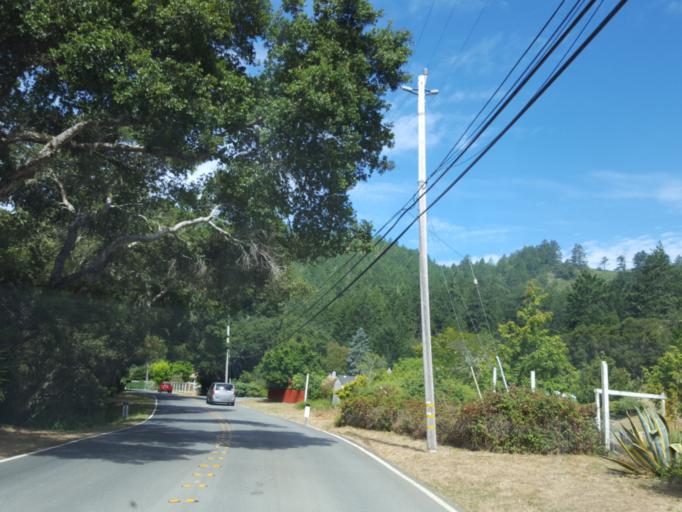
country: US
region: California
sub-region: San Mateo County
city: Portola Valley
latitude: 37.2615
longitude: -122.3331
